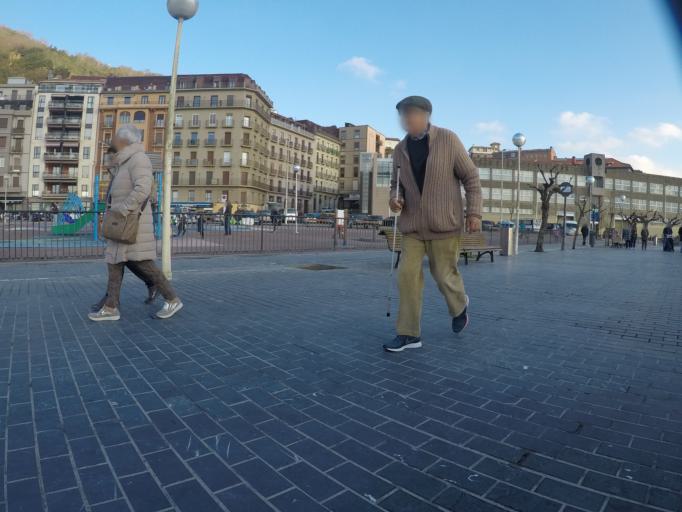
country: ES
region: Basque Country
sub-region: Provincia de Guipuzcoa
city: San Sebastian
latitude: 43.3280
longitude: -1.9714
